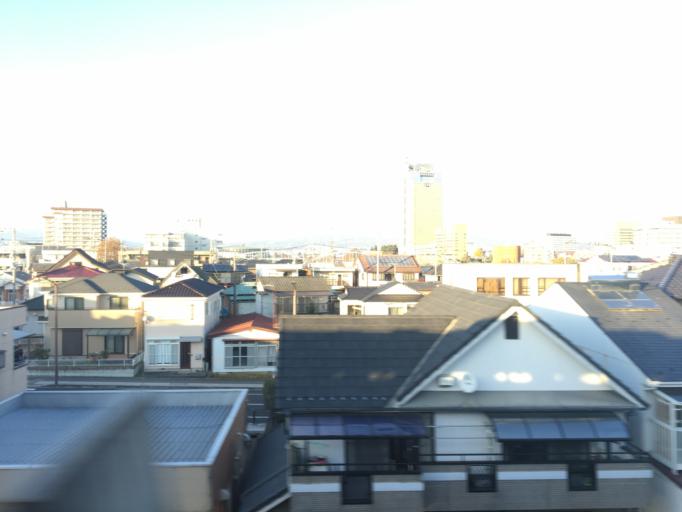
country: JP
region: Gunma
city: Maebashi-shi
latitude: 36.3830
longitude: 139.0567
